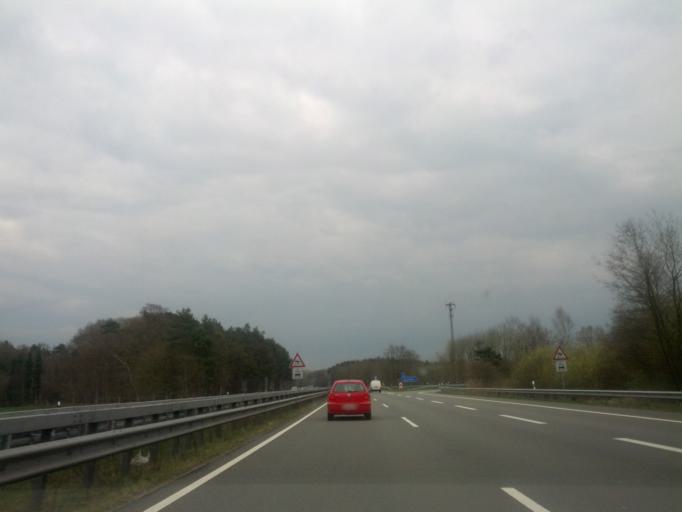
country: DE
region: Lower Saxony
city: Bad Zwischenahn
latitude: 53.2148
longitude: 8.0537
